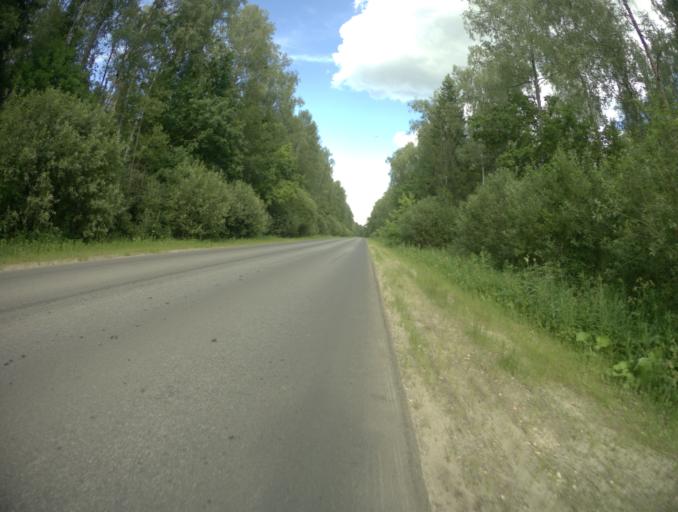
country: RU
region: Vladimir
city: Kommunar
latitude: 56.0700
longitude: 40.5167
